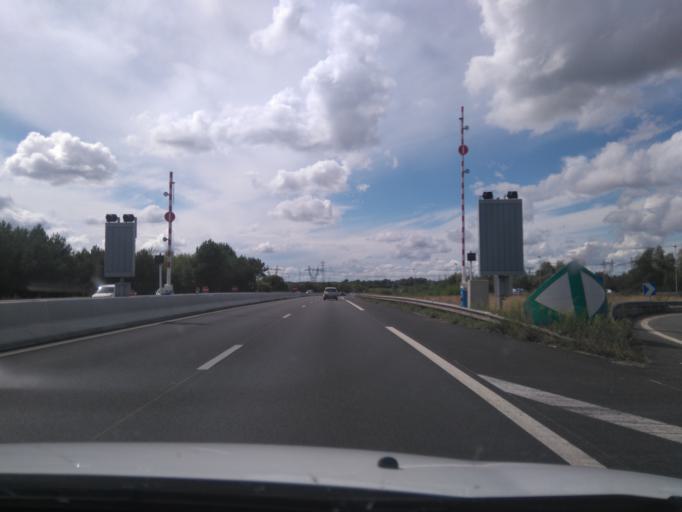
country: FR
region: Pays de la Loire
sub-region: Departement de la Loire-Atlantique
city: Bouguenais
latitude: 47.1804
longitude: -1.6083
